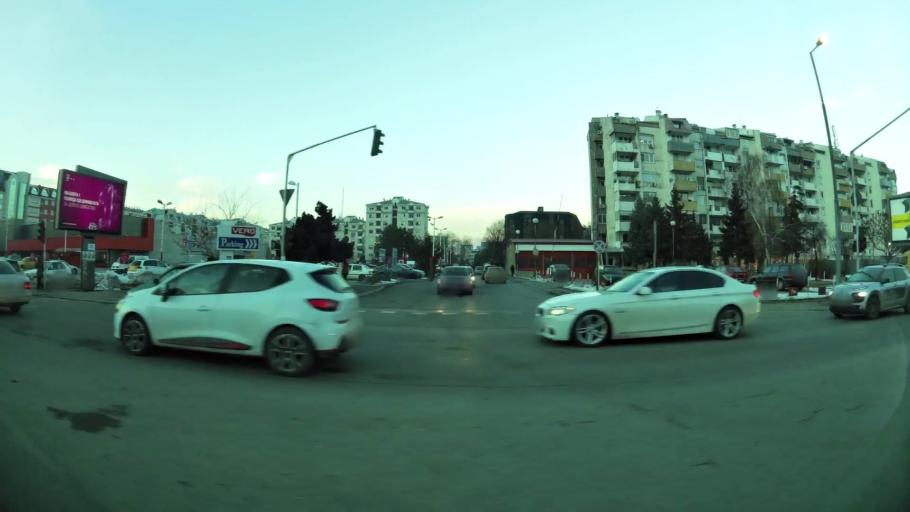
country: MK
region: Karpos
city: Skopje
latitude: 41.9962
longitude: 21.4057
